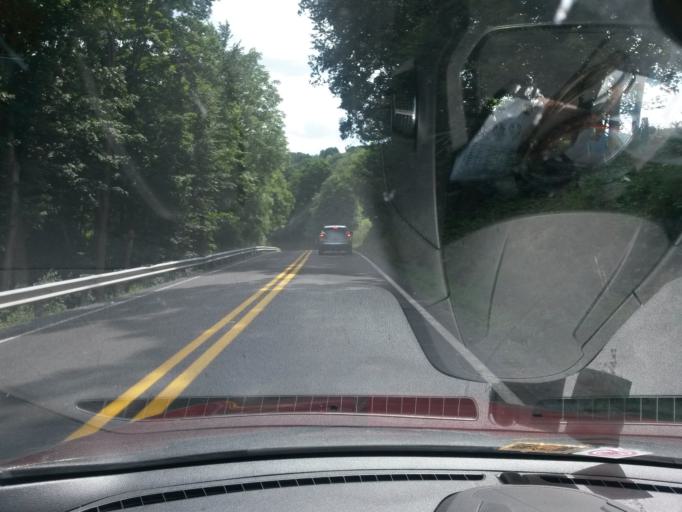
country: US
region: Virginia
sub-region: Highland County
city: Monterey
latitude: 38.5254
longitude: -79.4681
